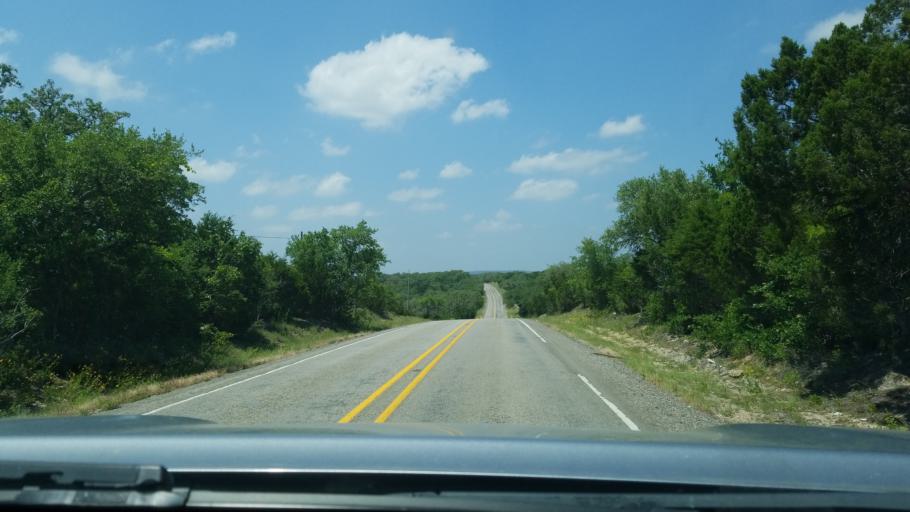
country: US
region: Texas
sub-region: Hays County
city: Woodcreek
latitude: 30.0544
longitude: -98.2046
